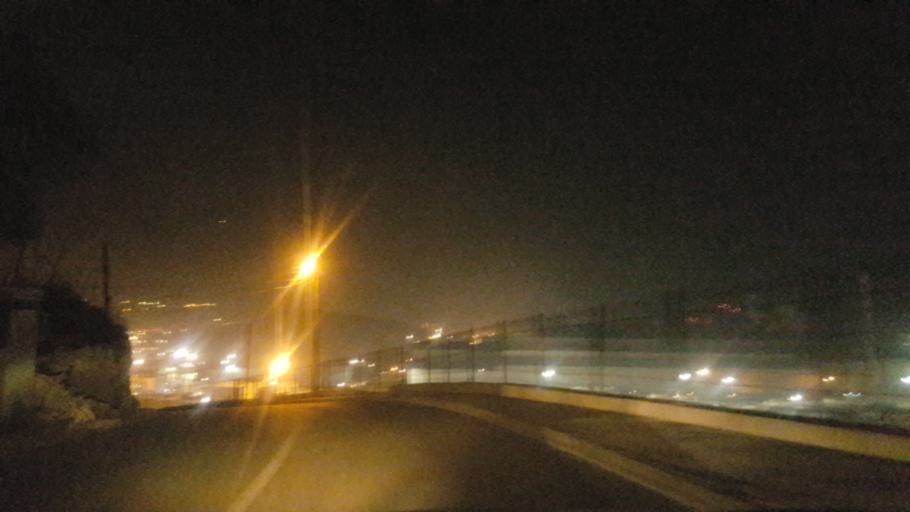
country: TR
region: Kocaeli
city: Tavsanli
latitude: 40.7699
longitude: 29.5214
